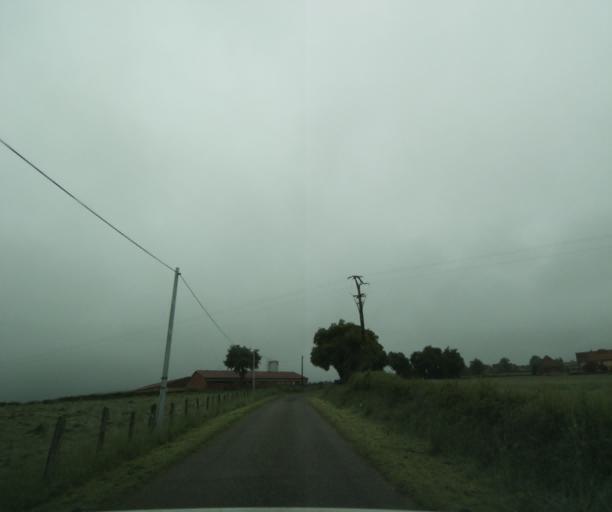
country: FR
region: Bourgogne
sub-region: Departement de Saone-et-Loire
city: Charolles
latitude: 46.3957
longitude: 4.3848
